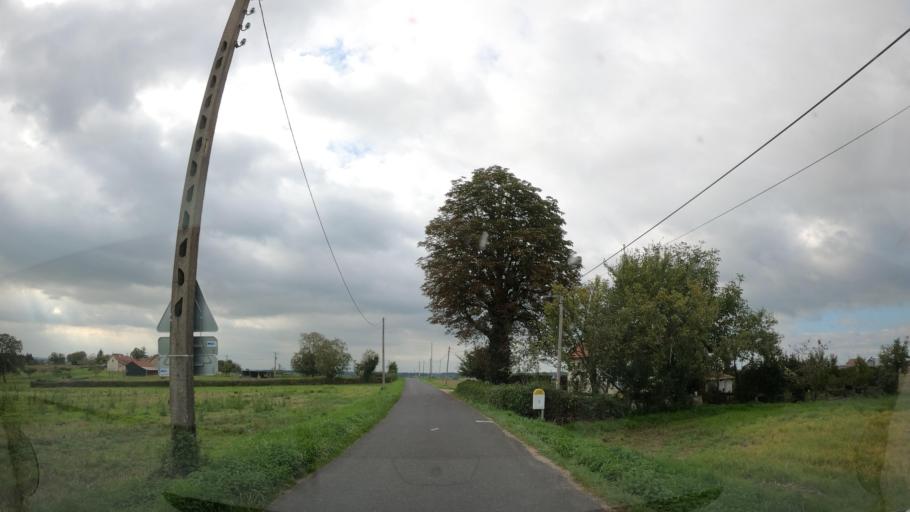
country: FR
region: Auvergne
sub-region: Departement de l'Allier
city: Lapalisse
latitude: 46.3534
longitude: 3.6179
